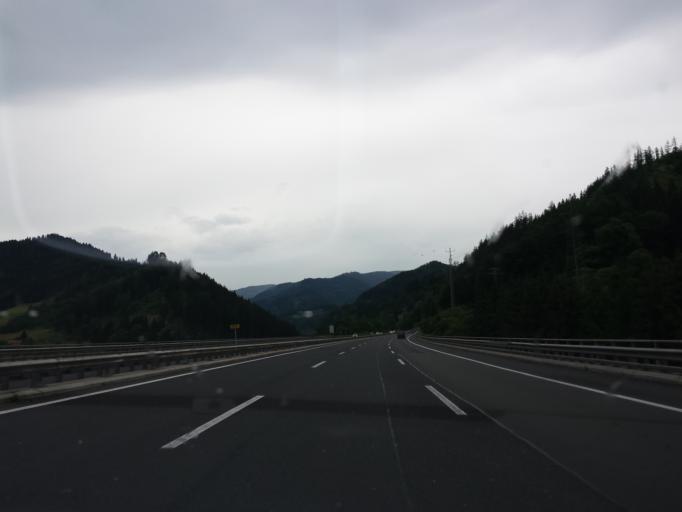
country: AT
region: Styria
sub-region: Politischer Bezirk Graz-Umgebung
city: Ubelbach
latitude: 47.2304
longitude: 15.2164
